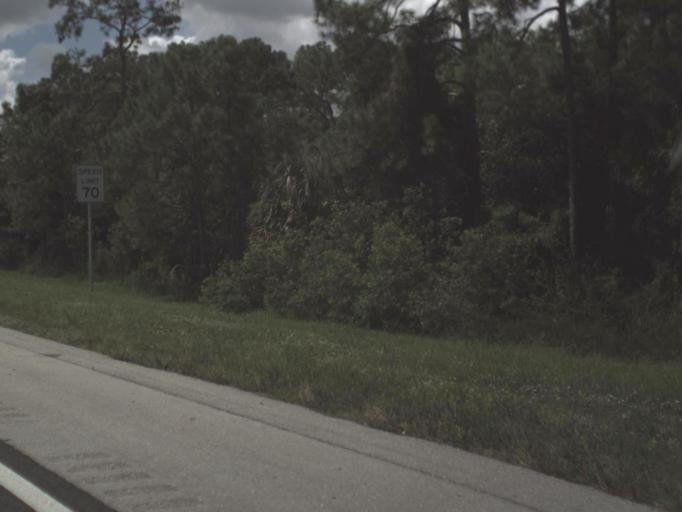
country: US
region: Florida
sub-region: Collier County
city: Vineyards
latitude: 26.1988
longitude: -81.7361
